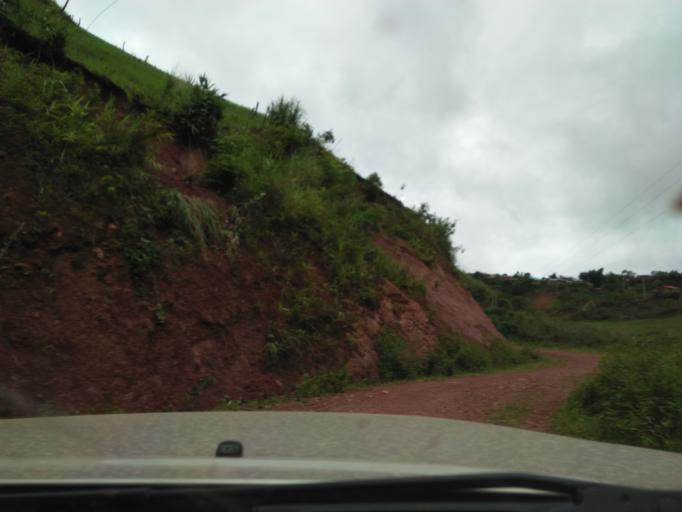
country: TH
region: Nan
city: Bo Kluea
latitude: 19.3795
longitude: 101.2093
